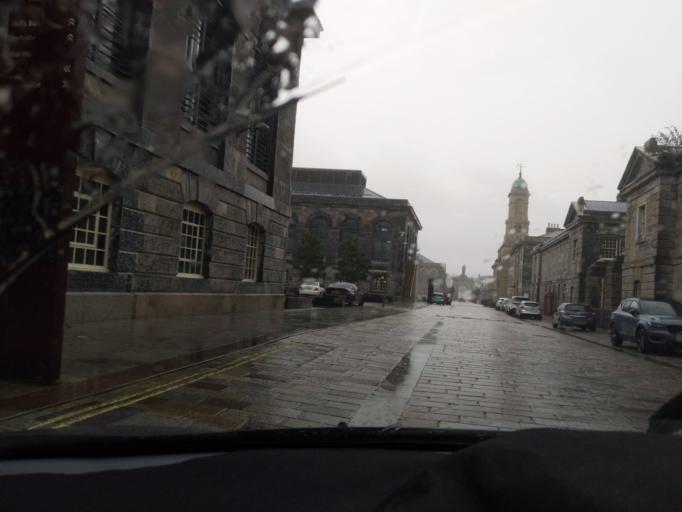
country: GB
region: England
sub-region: Cornwall
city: Millbrook
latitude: 50.3612
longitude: -4.1665
